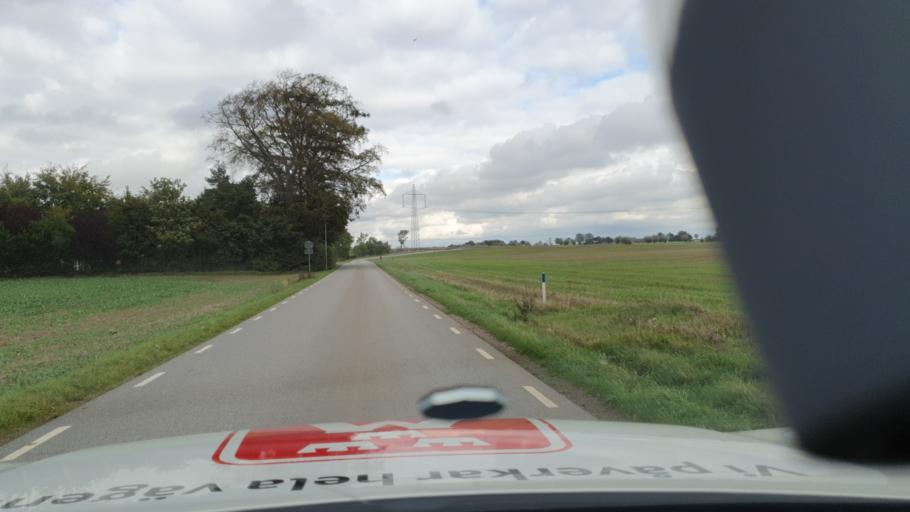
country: SE
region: Skane
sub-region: Vellinge Kommun
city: Vellinge
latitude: 55.4416
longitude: 13.0480
